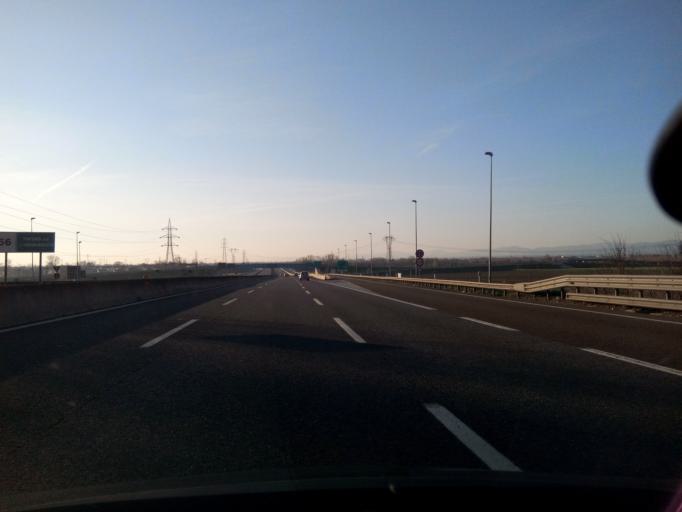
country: IT
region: Emilia-Romagna
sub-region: Provincia di Piacenza
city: Piacenza
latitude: 45.0608
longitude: 9.7391
